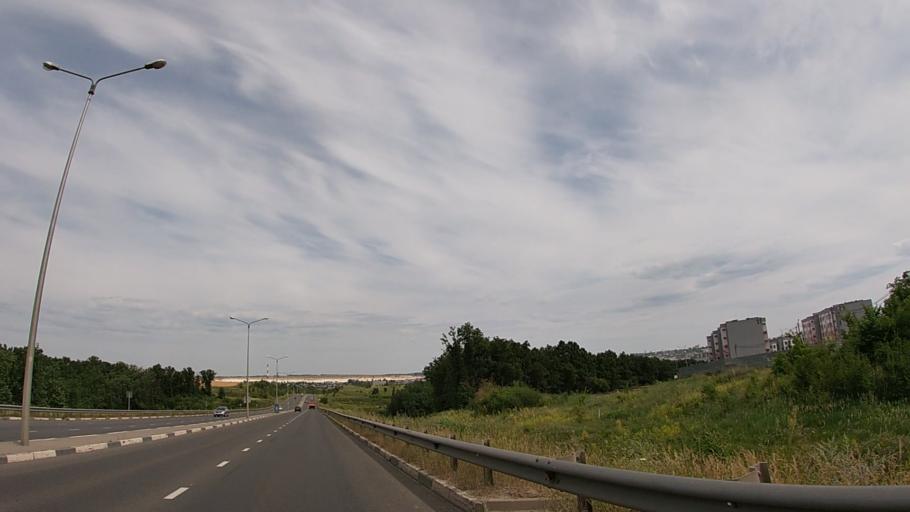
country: RU
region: Belgorod
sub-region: Belgorodskiy Rayon
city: Belgorod
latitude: 50.5982
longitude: 36.5304
